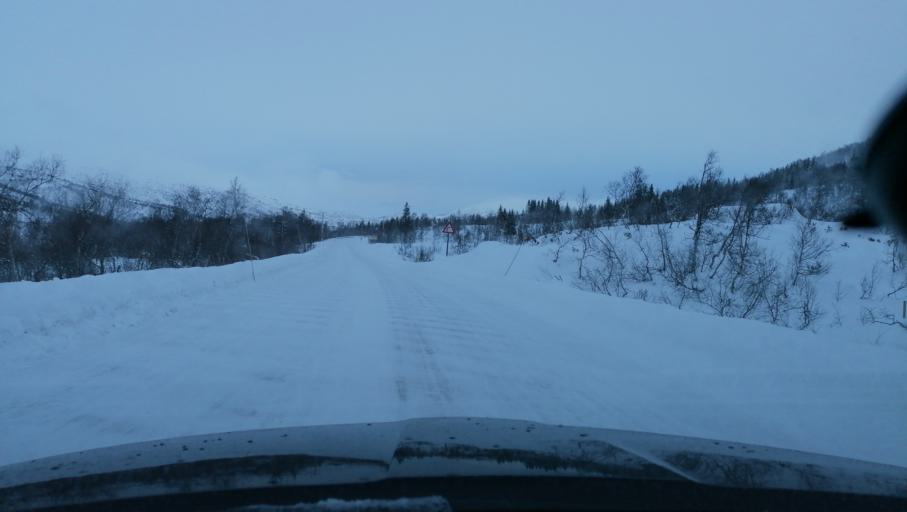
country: NO
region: Aust-Agder
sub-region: Bykle
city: Hovden
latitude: 59.6365
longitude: 7.4539
